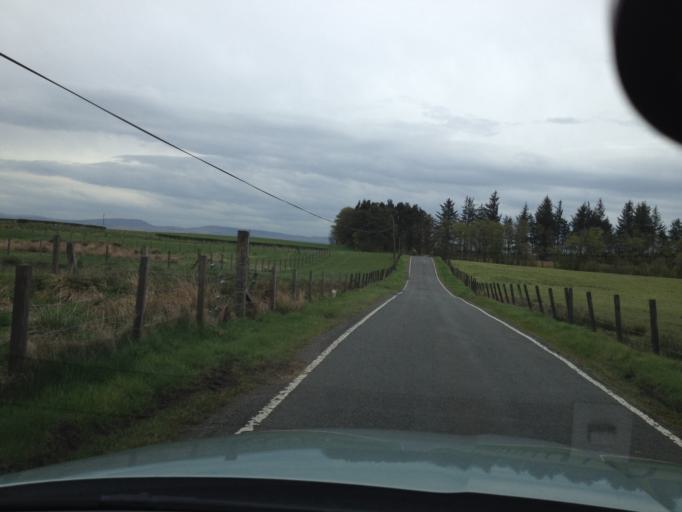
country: GB
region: Scotland
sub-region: West Lothian
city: Linlithgow
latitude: 55.9314
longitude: -3.5787
